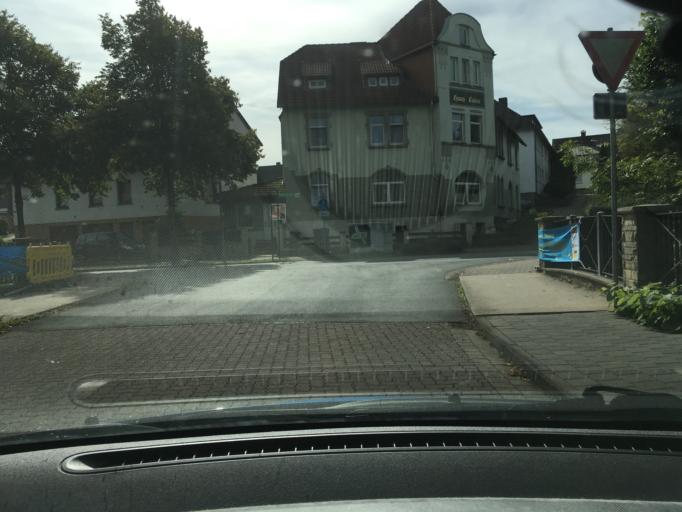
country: DE
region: Lower Saxony
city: Bad Munder am Deister
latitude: 52.1941
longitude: 9.4611
